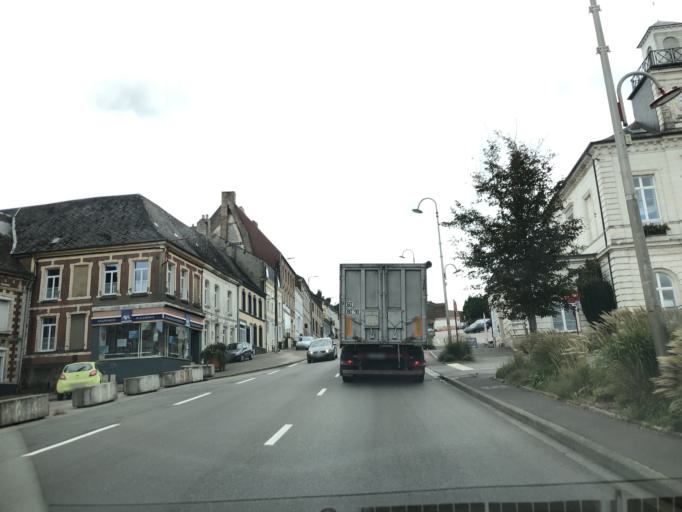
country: FR
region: Nord-Pas-de-Calais
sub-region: Departement du Pas-de-Calais
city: Fruges
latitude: 50.5134
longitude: 2.1344
